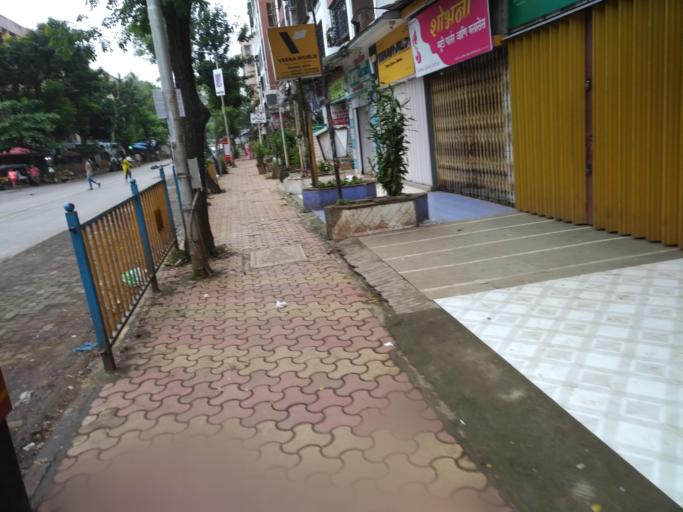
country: IN
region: Maharashtra
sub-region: Mumbai Suburban
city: Borivli
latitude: 19.2348
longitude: 72.8641
